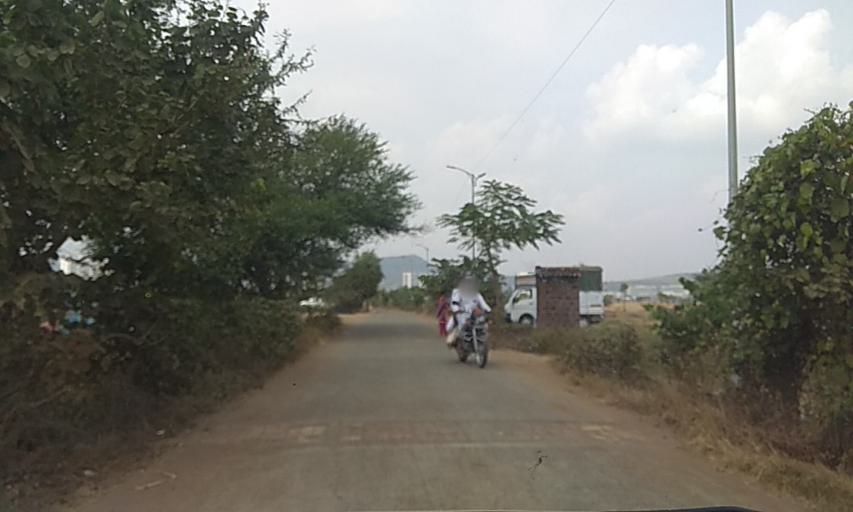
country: IN
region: Maharashtra
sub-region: Pune Division
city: Pimpri
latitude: 18.5788
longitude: 73.7082
